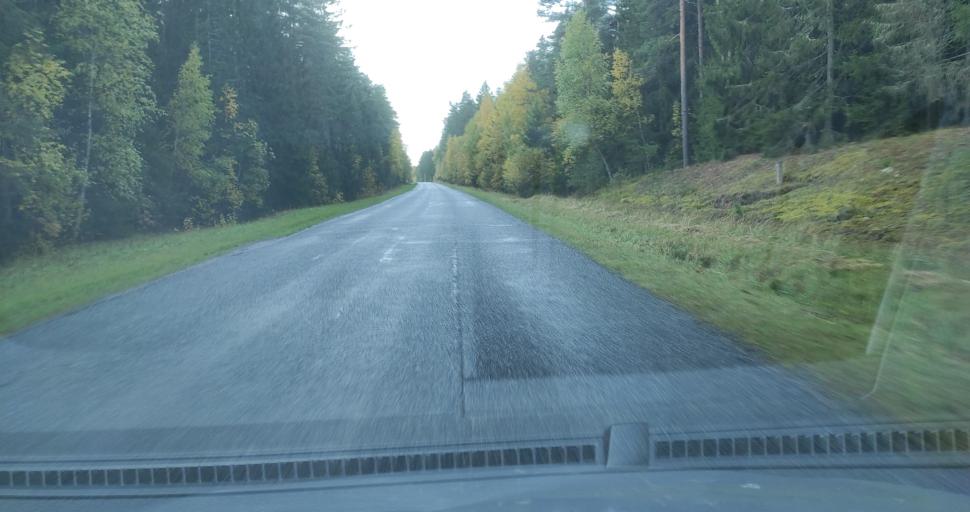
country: LV
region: Skrunda
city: Skrunda
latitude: 56.6432
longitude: 22.0093
